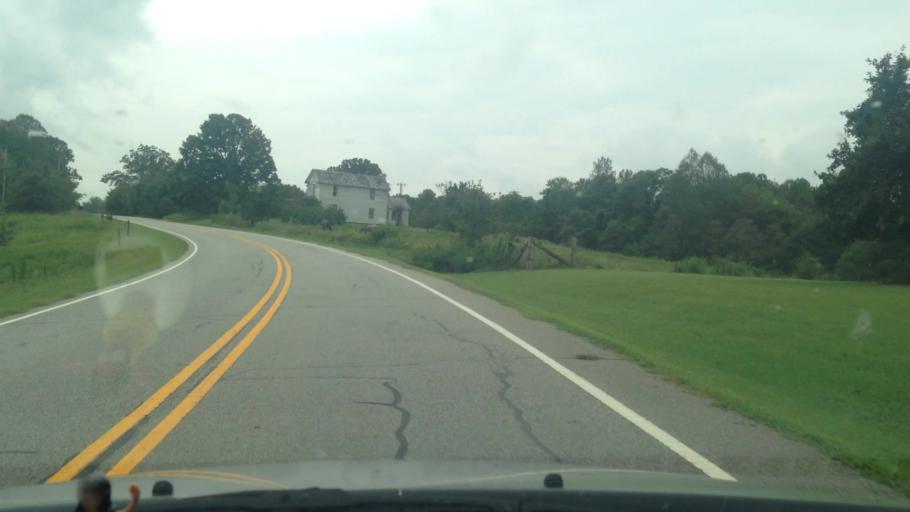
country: US
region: North Carolina
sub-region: Stokes County
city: Danbury
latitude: 36.4222
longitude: -80.1107
